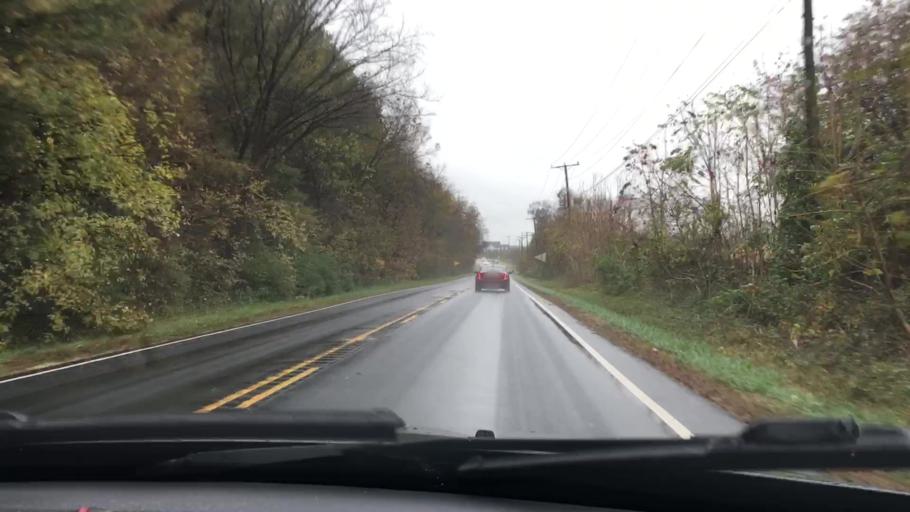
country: US
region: Virginia
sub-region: Loudoun County
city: Leesburg
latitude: 39.1797
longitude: -77.5360
